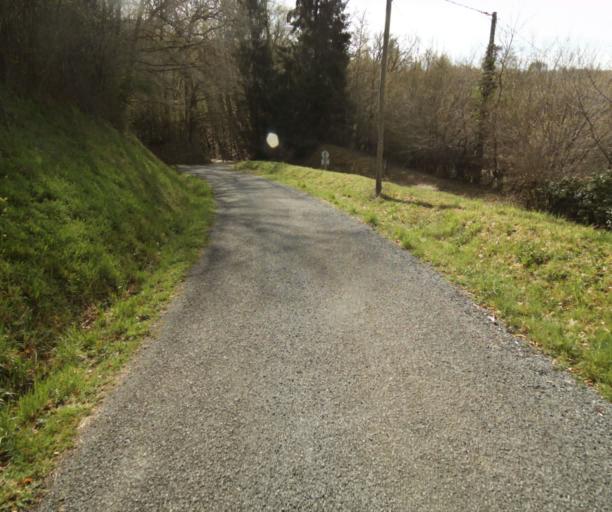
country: FR
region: Limousin
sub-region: Departement de la Correze
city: Laguenne
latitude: 45.2430
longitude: 1.8084
